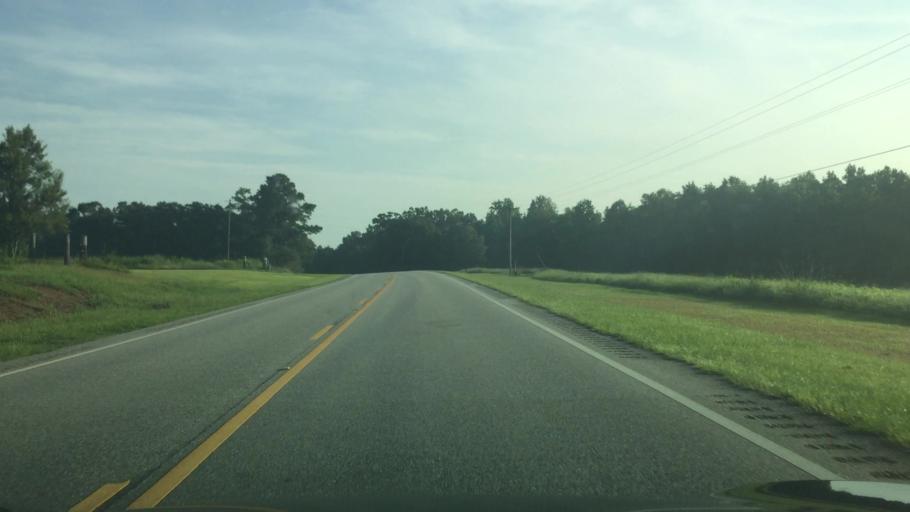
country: US
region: Alabama
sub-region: Covington County
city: Andalusia
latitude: 31.1519
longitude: -86.4586
